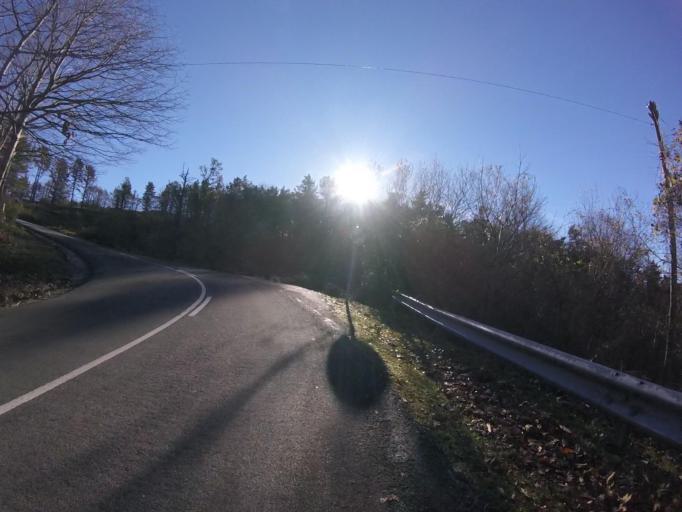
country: ES
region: Basque Country
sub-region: Provincia de Guipuzcoa
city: Irun
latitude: 43.3126
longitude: -1.7580
